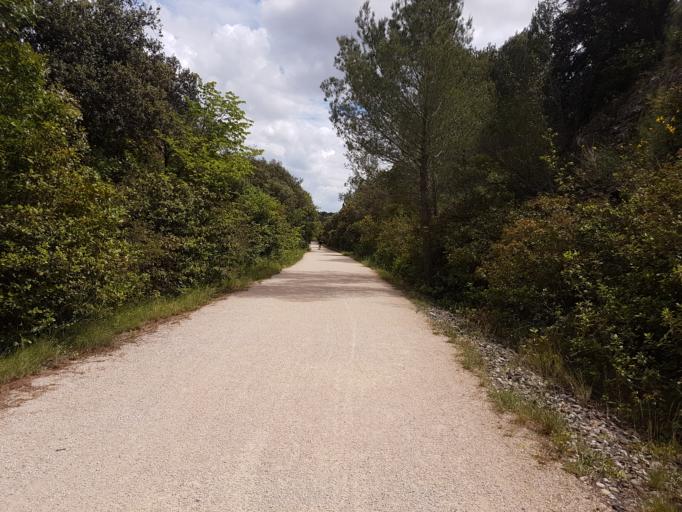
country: FR
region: Languedoc-Roussillon
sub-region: Departement du Gard
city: Vallabregues
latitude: 43.8307
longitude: 4.6182
